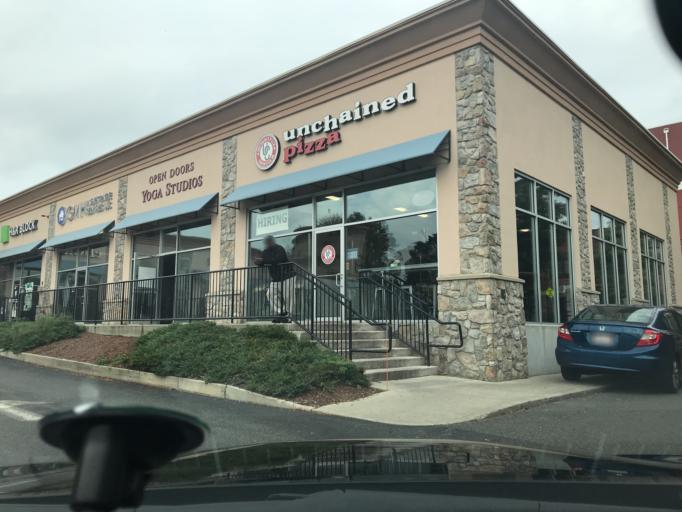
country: US
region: Massachusetts
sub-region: Suffolk County
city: South Boston
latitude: 42.2914
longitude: -71.0465
